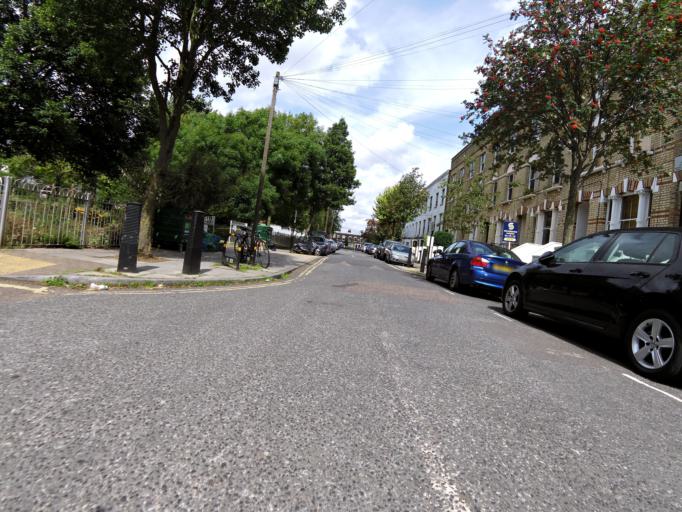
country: GB
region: England
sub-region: Greater London
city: Holloway
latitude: 51.5633
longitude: -0.1273
